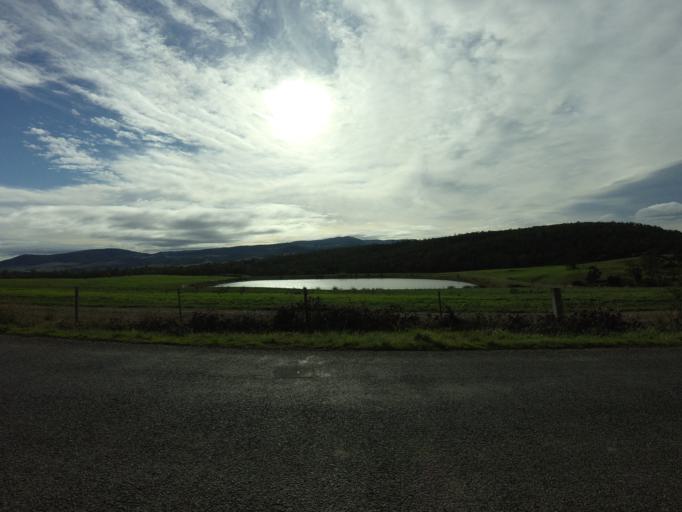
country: AU
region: Tasmania
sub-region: Derwent Valley
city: New Norfolk
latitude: -42.7806
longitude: 146.9898
